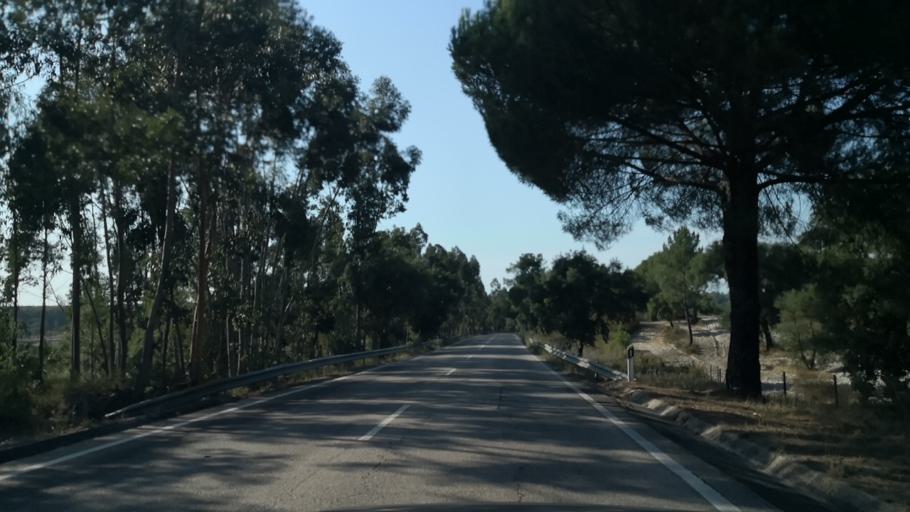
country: PT
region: Santarem
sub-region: Coruche
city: Coruche
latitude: 38.9863
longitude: -8.5504
